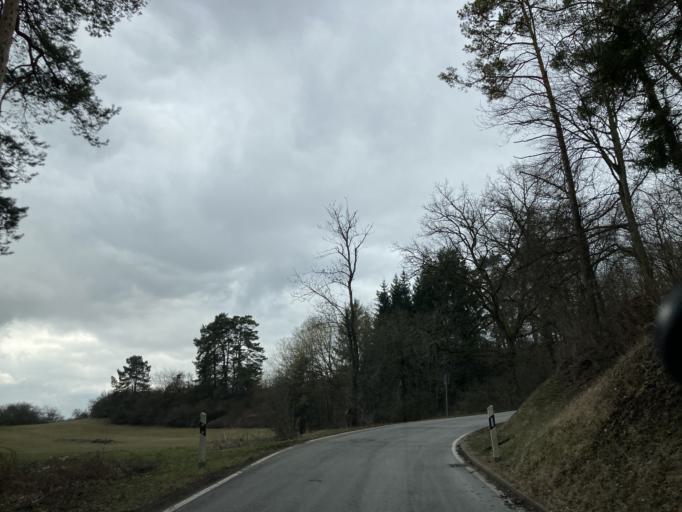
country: DE
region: Baden-Wuerttemberg
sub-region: Tuebingen Region
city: Hirrlingen
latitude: 48.4290
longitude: 8.8270
